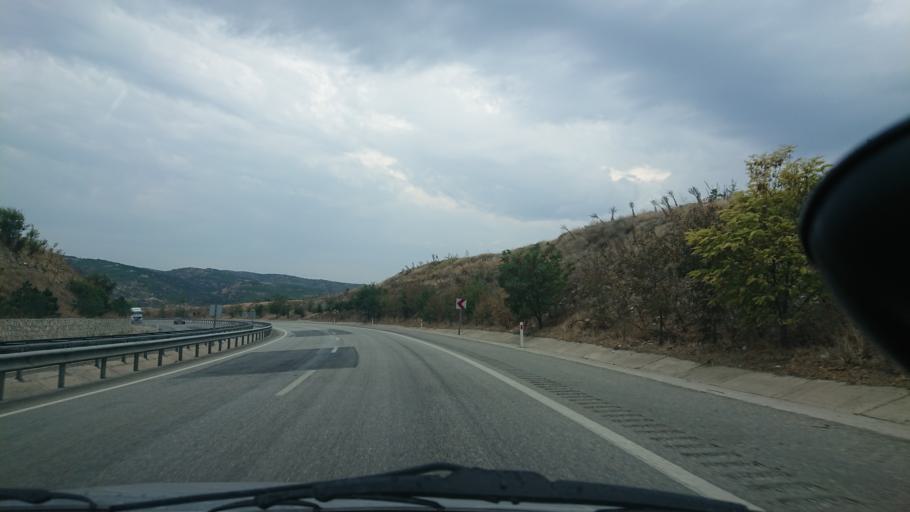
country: TR
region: Manisa
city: Selendi
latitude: 38.6009
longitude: 28.8128
